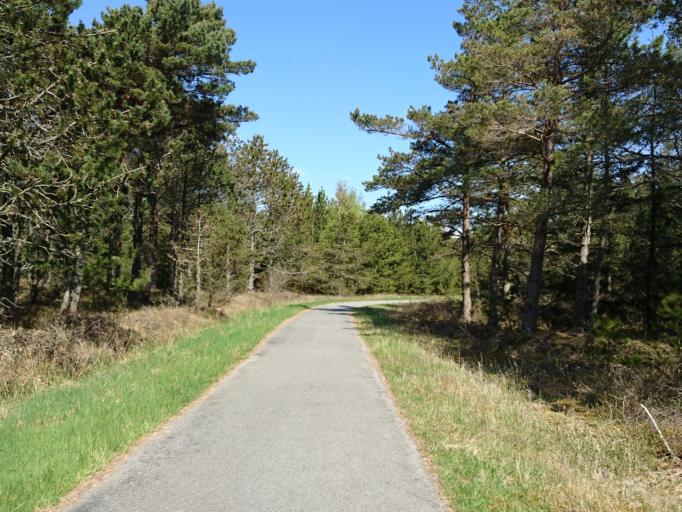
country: DK
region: North Denmark
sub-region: Frederikshavn Kommune
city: Skagen
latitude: 57.6992
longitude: 10.5119
